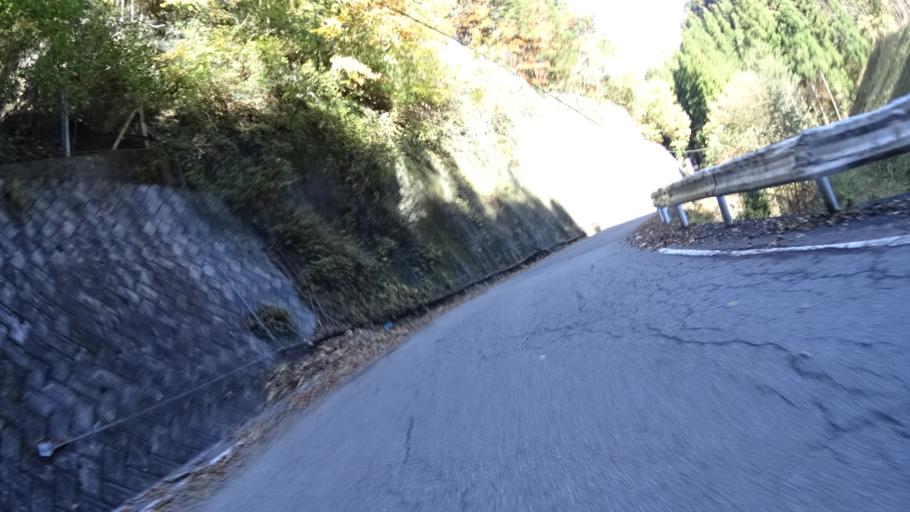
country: JP
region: Yamanashi
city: Otsuki
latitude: 35.7780
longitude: 138.9204
